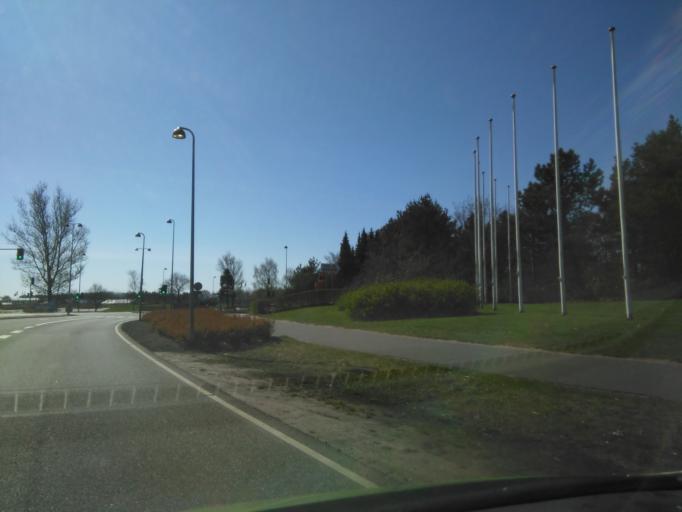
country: DK
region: South Denmark
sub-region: Billund Kommune
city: Billund
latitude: 55.7345
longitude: 9.1335
